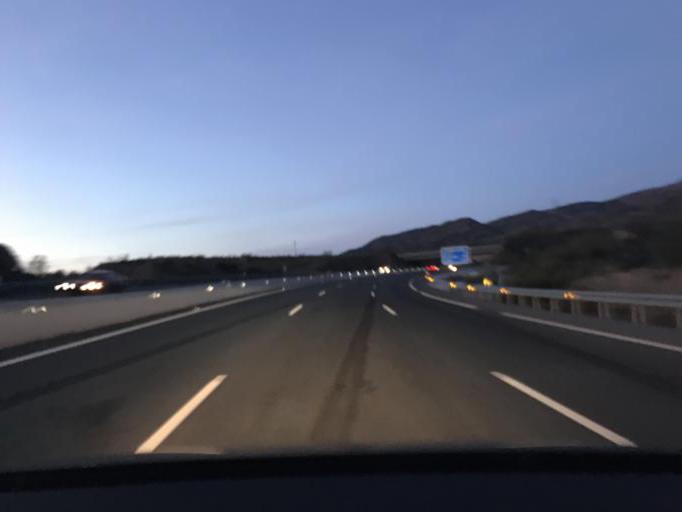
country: ES
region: Andalusia
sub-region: Provincia de Granada
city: Lanjaron
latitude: 36.9067
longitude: -3.5269
